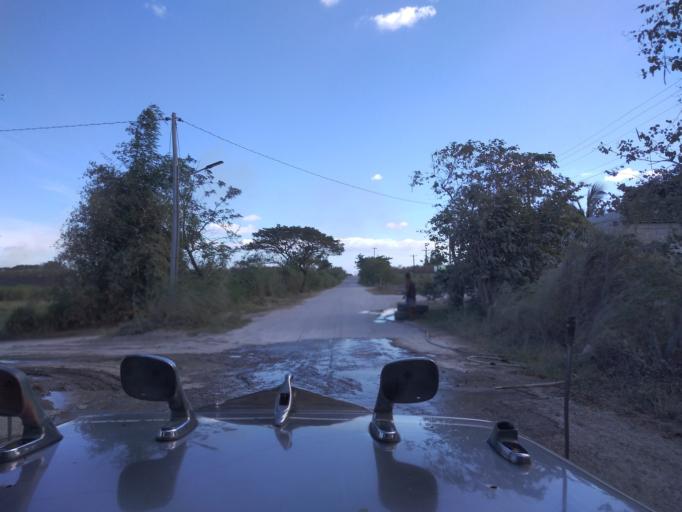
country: PH
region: Central Luzon
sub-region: Province of Pampanga
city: Magliman
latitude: 15.0360
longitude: 120.6326
